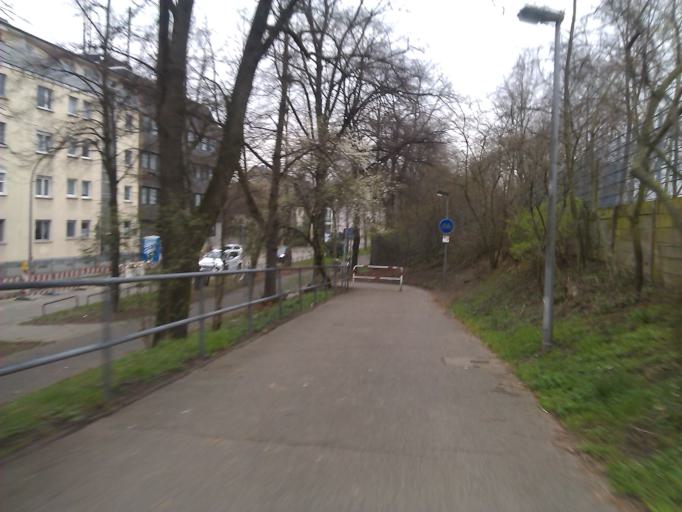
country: DE
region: North Rhine-Westphalia
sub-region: Regierungsbezirk Koln
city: Riehl
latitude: 50.9856
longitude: 6.9670
